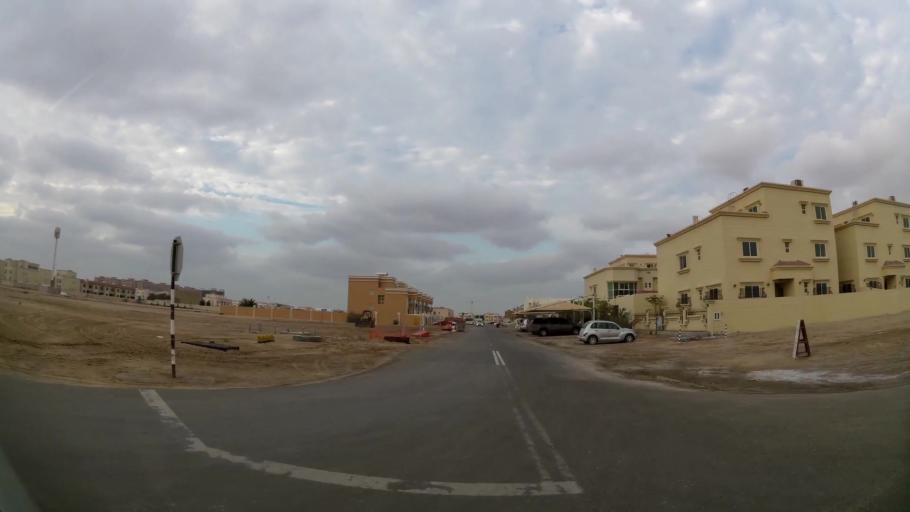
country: AE
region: Abu Dhabi
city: Abu Dhabi
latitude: 24.3638
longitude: 54.5465
